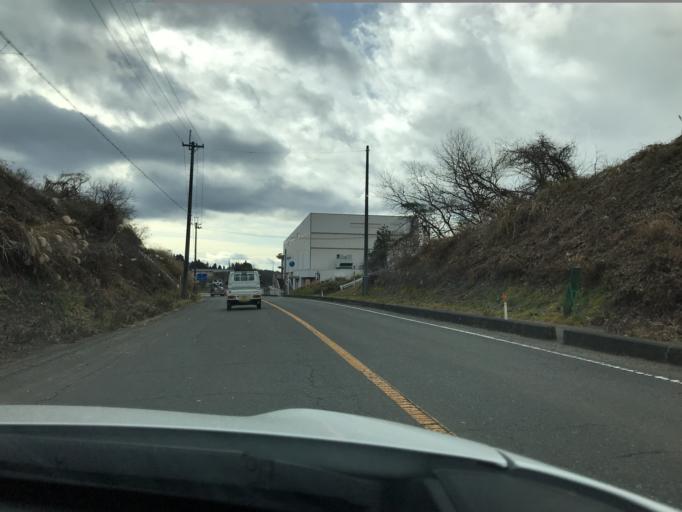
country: JP
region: Fukushima
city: Nihommatsu
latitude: 37.5994
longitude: 140.5807
